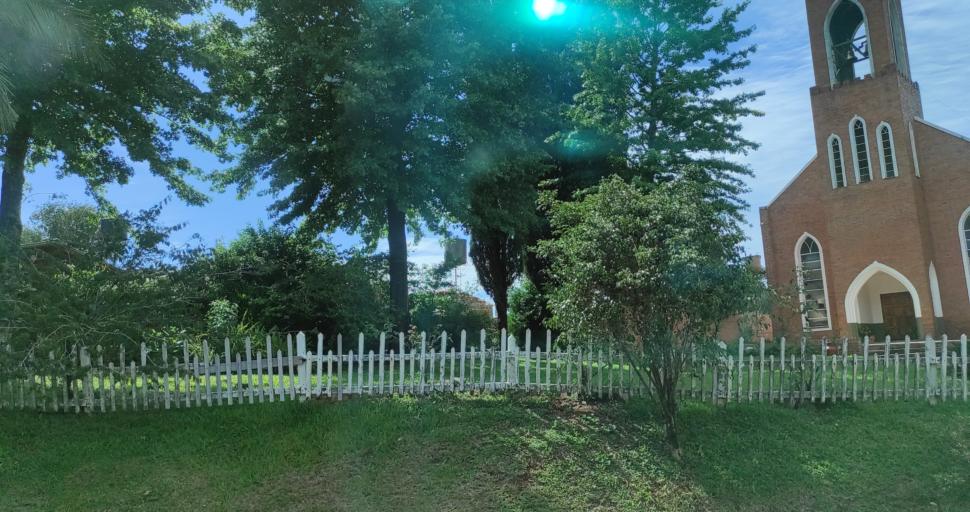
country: AR
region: Misiones
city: Dos de Mayo
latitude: -27.0178
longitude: -54.6862
